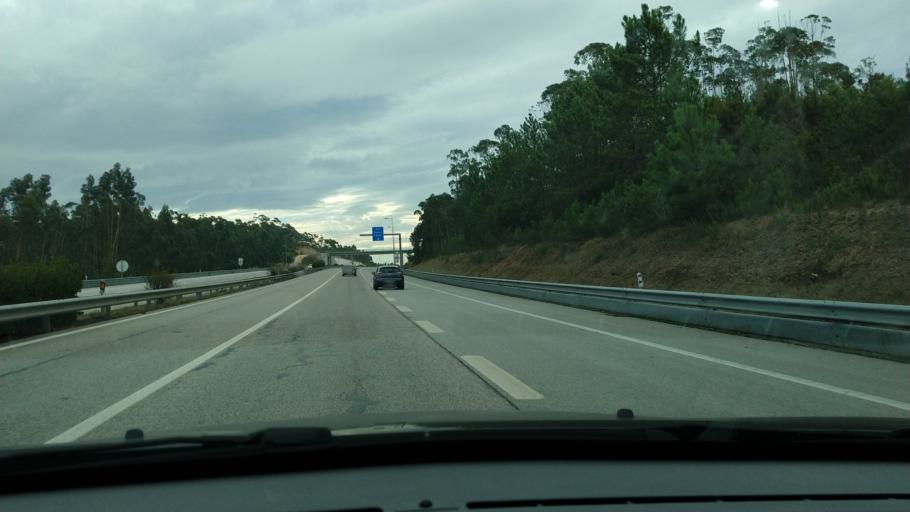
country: PT
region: Coimbra
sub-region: Figueira da Foz
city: Alhadas
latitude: 40.1537
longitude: -8.7899
